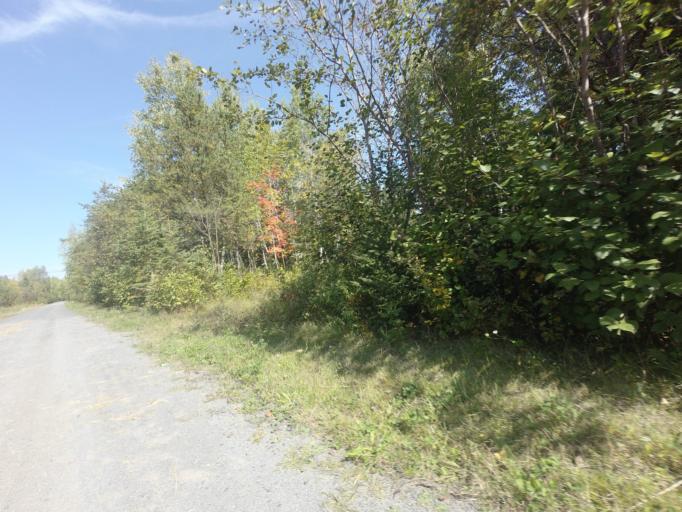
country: CA
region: Quebec
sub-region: Laurentides
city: Sainte-Agathe-des-Monts
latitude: 46.0553
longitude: -74.2836
